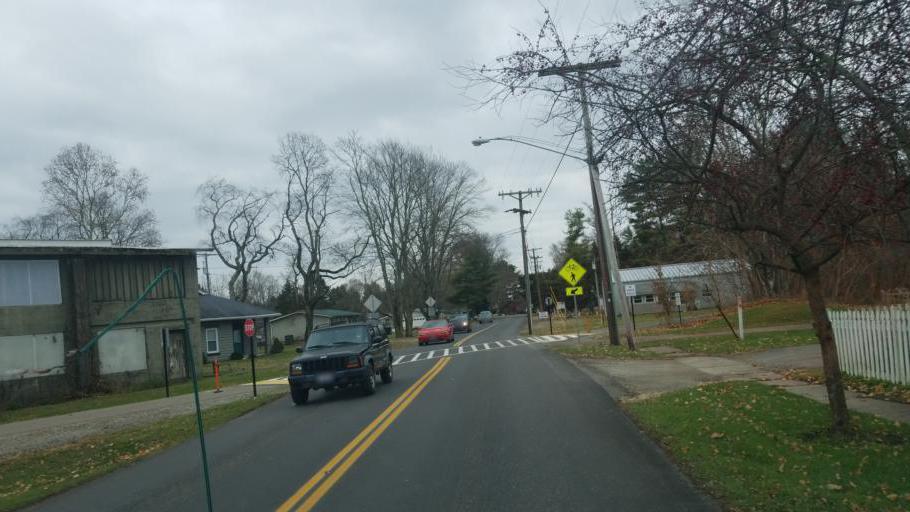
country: US
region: Ohio
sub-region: Knox County
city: Fredericktown
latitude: 40.4790
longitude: -82.5383
